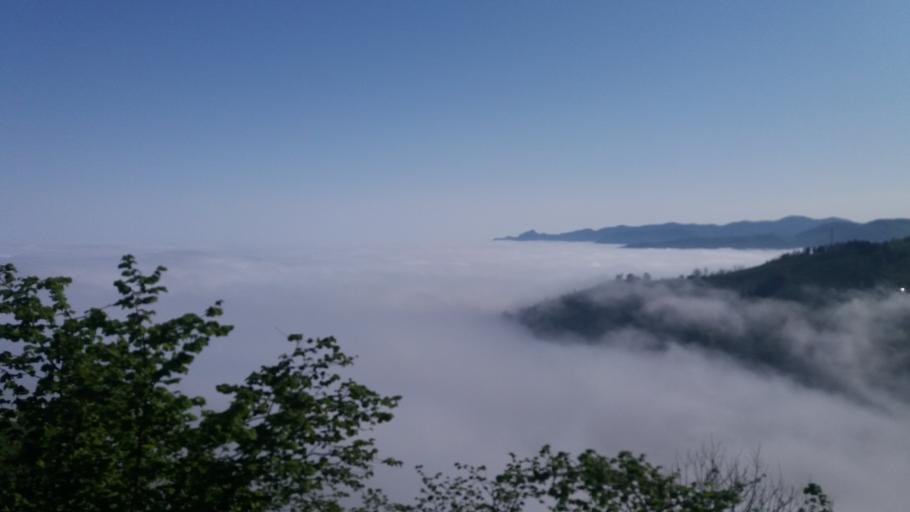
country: TR
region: Ordu
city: Kabaduz
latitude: 40.8501
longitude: 37.8917
